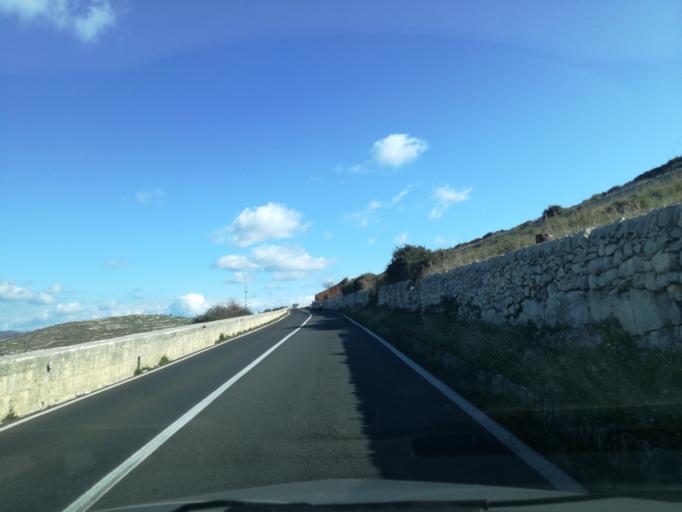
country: IT
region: Sicily
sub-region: Ragusa
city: Comiso
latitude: 36.9405
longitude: 14.6327
